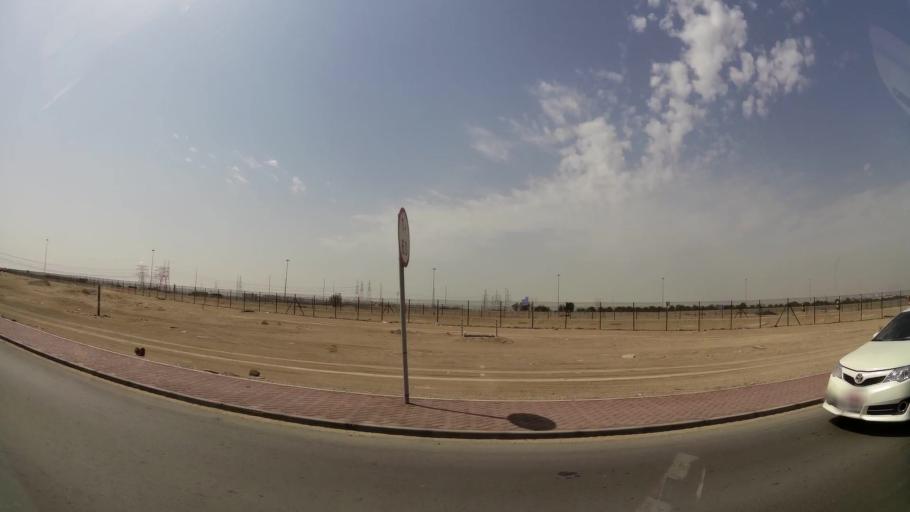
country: AE
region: Abu Dhabi
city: Abu Dhabi
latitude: 24.3126
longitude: 54.5305
